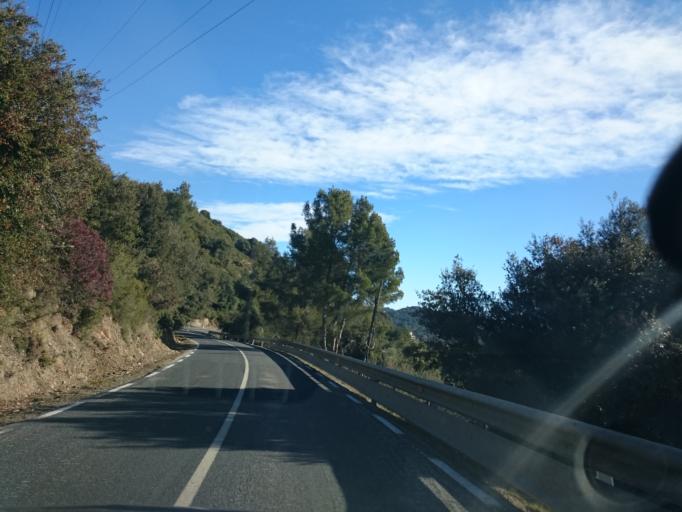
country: ES
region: Catalonia
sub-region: Provincia de Barcelona
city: Sant Just Desvern
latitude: 41.4073
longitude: 2.0833
